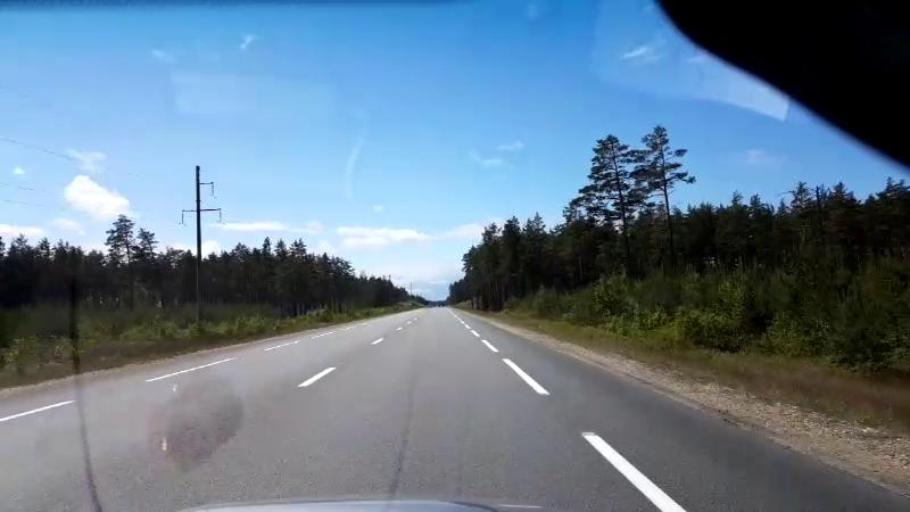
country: LV
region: Saulkrastu
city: Saulkrasti
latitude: 57.2130
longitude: 24.3953
